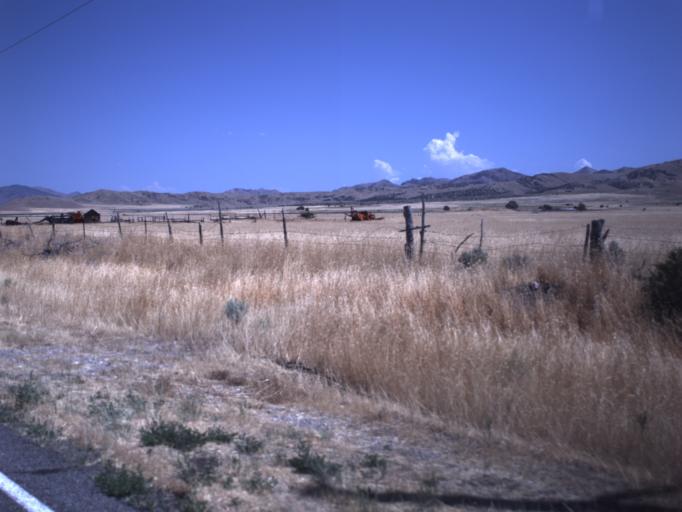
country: US
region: Utah
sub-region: Millard County
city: Delta
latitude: 39.3881
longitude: -112.3357
